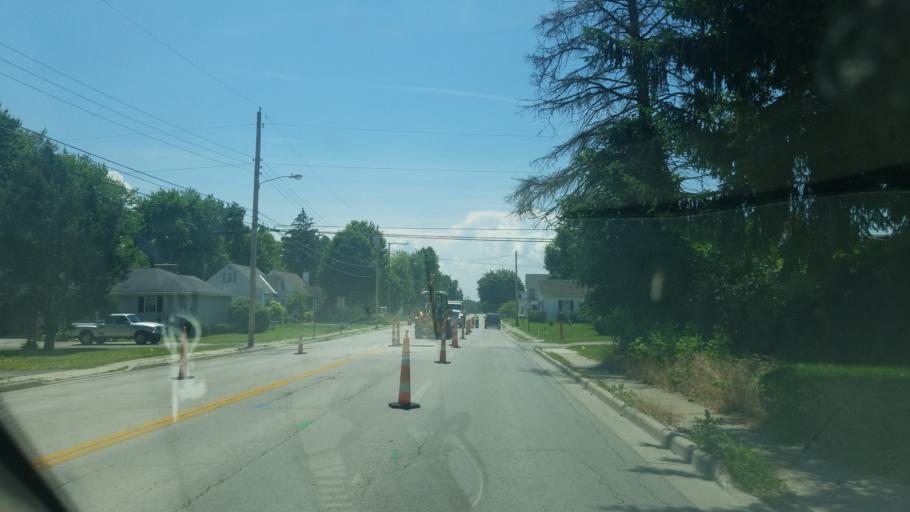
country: US
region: Ohio
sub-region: Hancock County
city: Findlay
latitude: 41.0274
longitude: -83.6412
